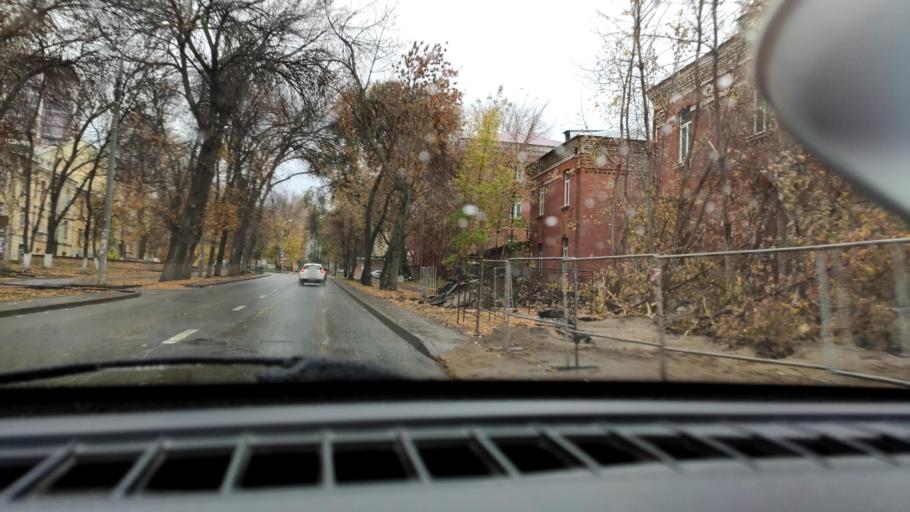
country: RU
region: Samara
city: Samara
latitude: 53.2157
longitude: 50.1556
